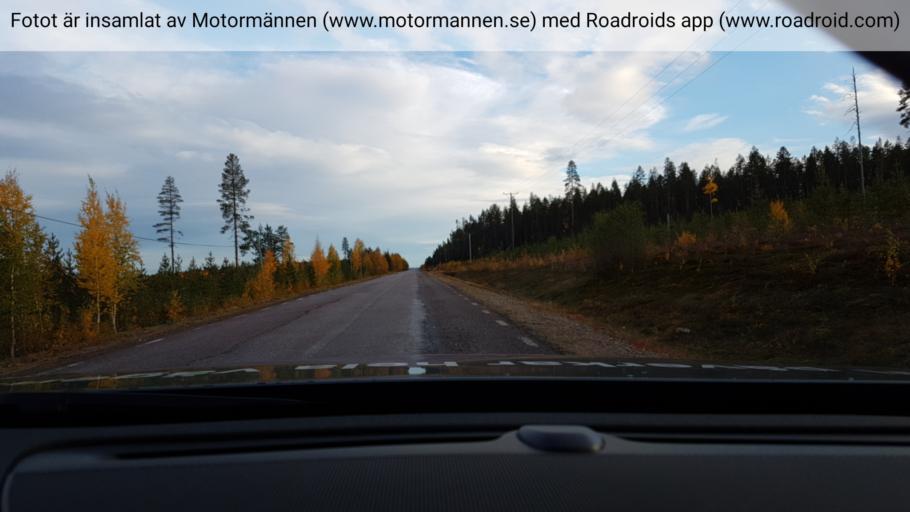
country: SE
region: Norrbotten
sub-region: Overkalix Kommun
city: OEverkalix
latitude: 67.0311
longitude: 22.5082
